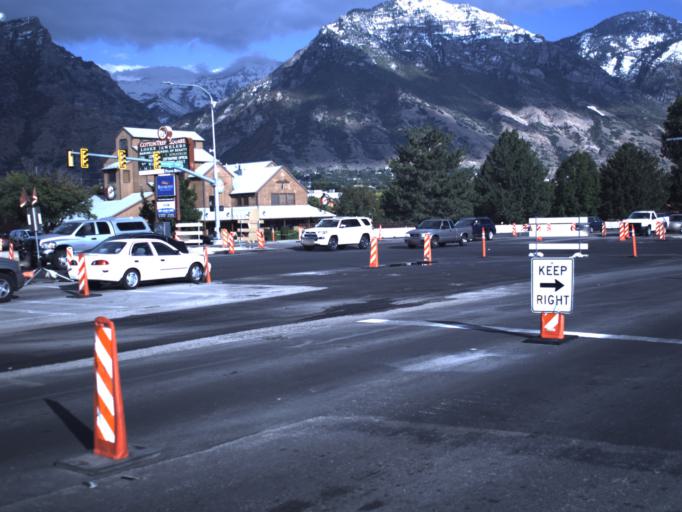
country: US
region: Utah
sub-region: Utah County
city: Provo
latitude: 40.2631
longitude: -111.6679
